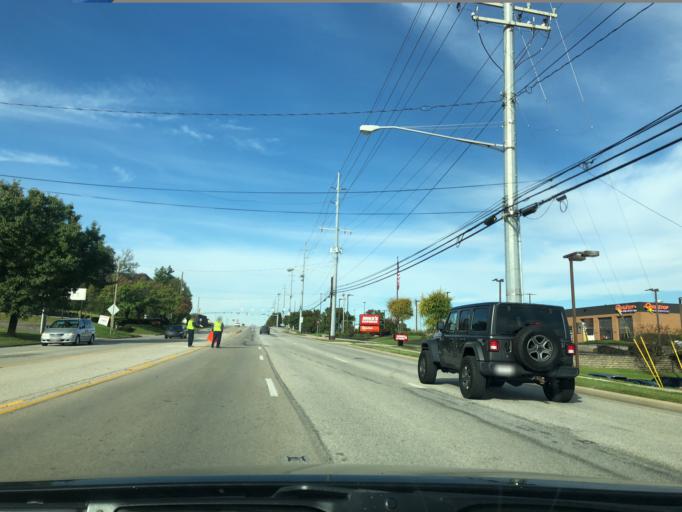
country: US
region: Ohio
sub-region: Hamilton County
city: Glendale
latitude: 39.2863
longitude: -84.4500
